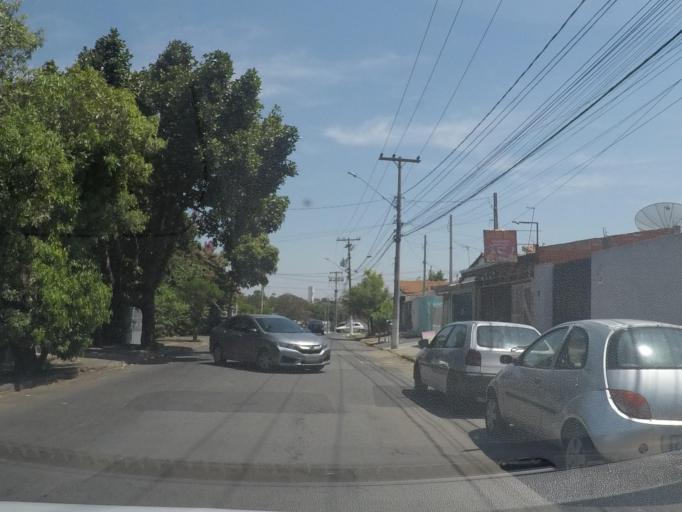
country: BR
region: Sao Paulo
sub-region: Hortolandia
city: Hortolandia
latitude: -22.8586
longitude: -47.2121
